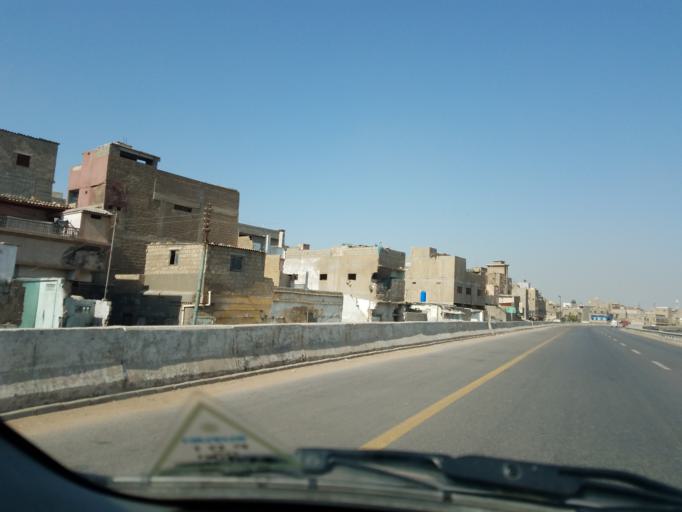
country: PK
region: Sindh
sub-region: Karachi District
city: Karachi
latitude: 24.8877
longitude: 67.0243
